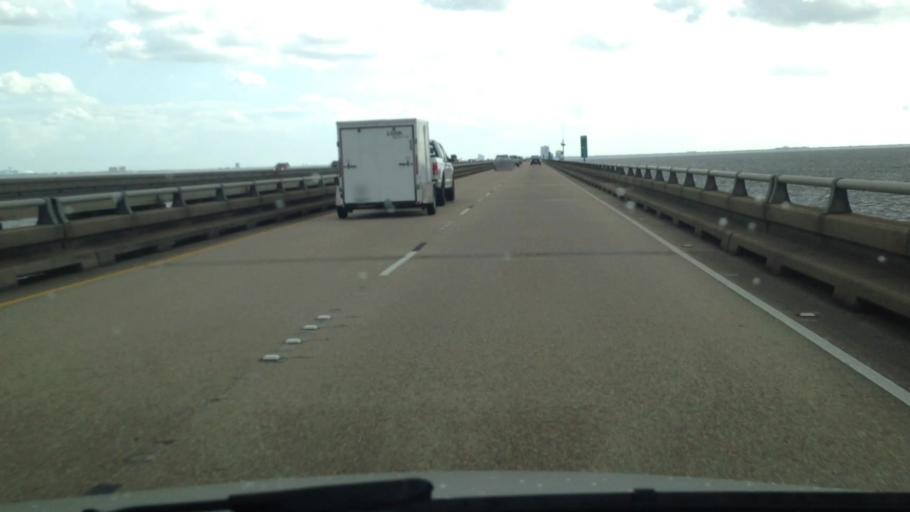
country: US
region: Louisiana
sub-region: Jefferson Parish
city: Metairie
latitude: 30.0984
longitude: -90.1407
